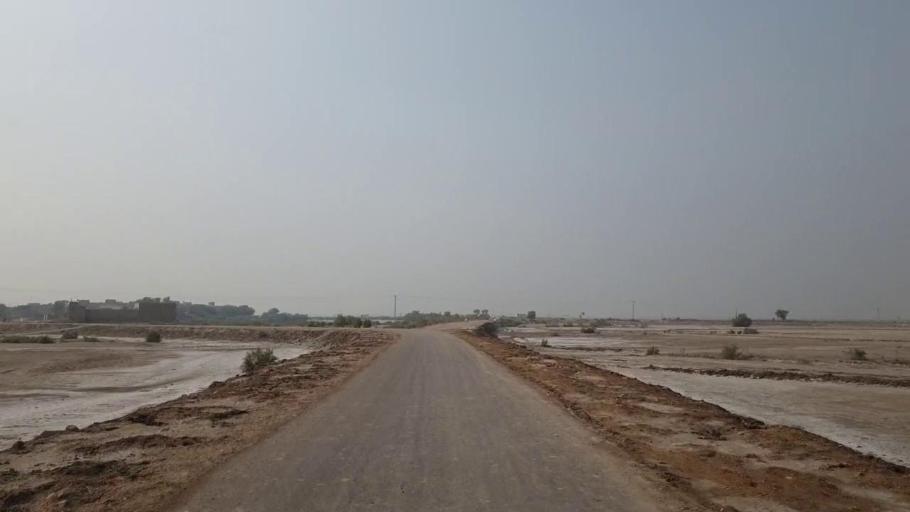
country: PK
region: Sindh
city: Bhan
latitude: 26.5094
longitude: 67.6796
